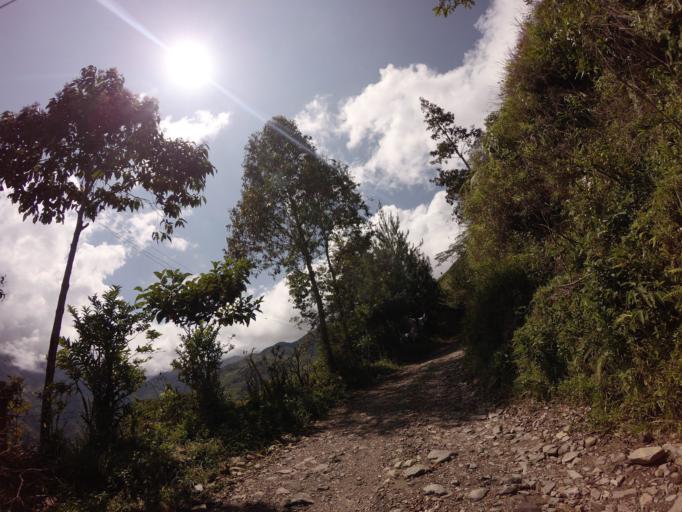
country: CO
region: Caldas
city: Pensilvania
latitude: 5.4815
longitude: -75.1798
